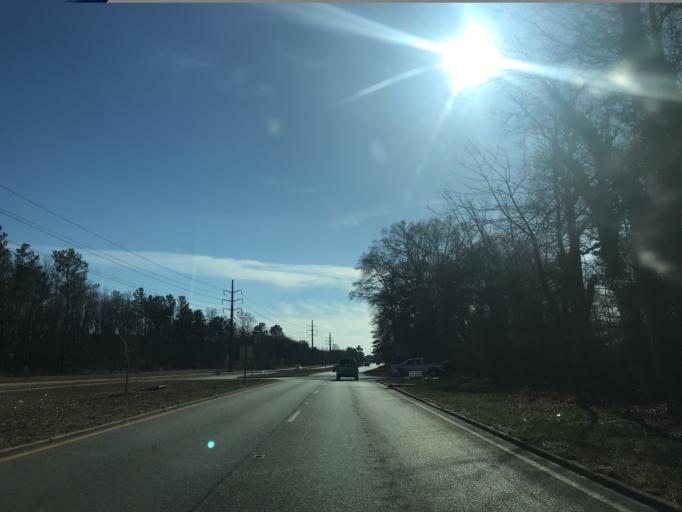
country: US
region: Maryland
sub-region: Charles County
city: Saint Charles
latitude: 38.5906
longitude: -76.9159
